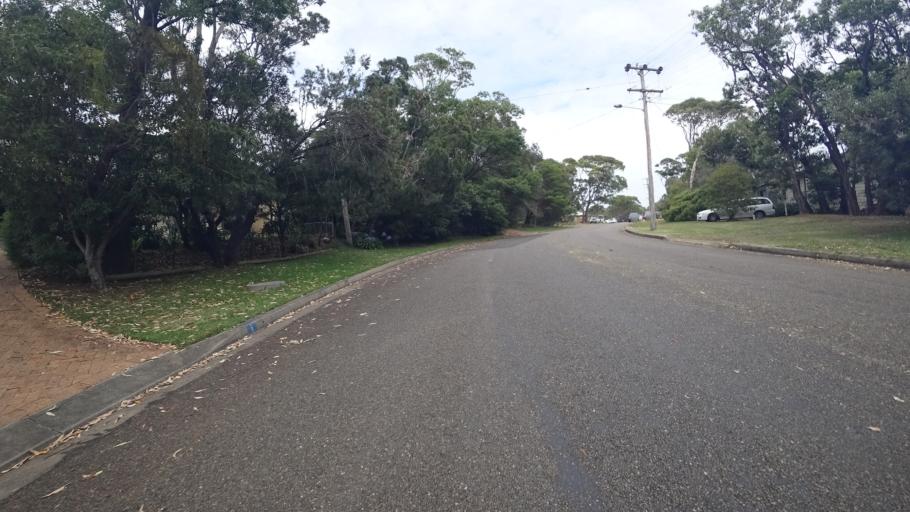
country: AU
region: New South Wales
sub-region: Shoalhaven Shire
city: Milton
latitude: -35.2558
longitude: 150.5209
